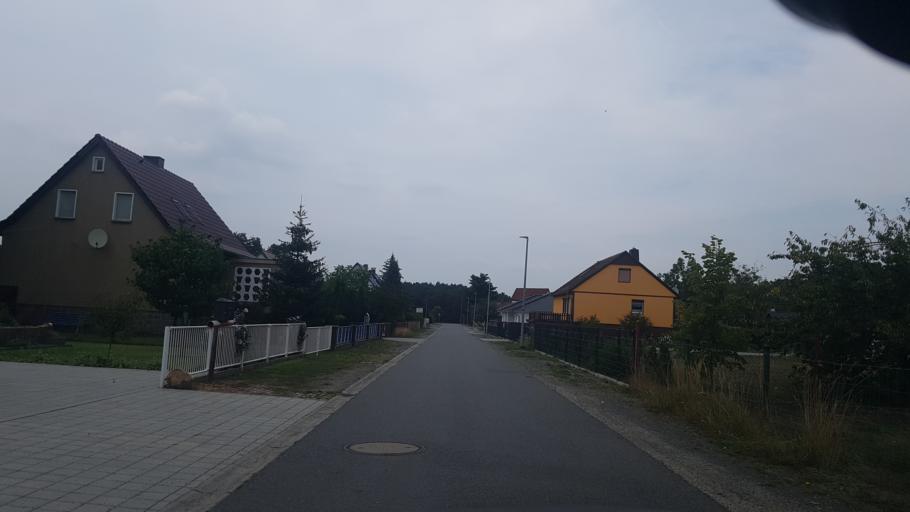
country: DE
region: Brandenburg
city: Guteborn
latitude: 51.4276
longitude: 13.9134
